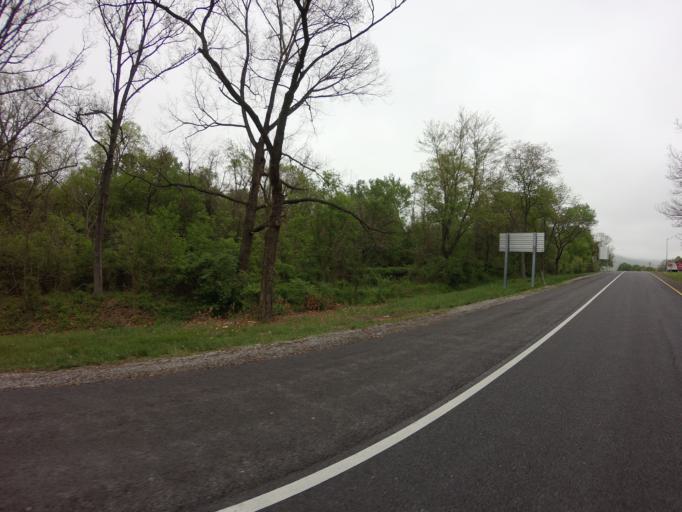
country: US
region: Maryland
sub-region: Washington County
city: Robinwood
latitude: 39.5858
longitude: -77.6380
